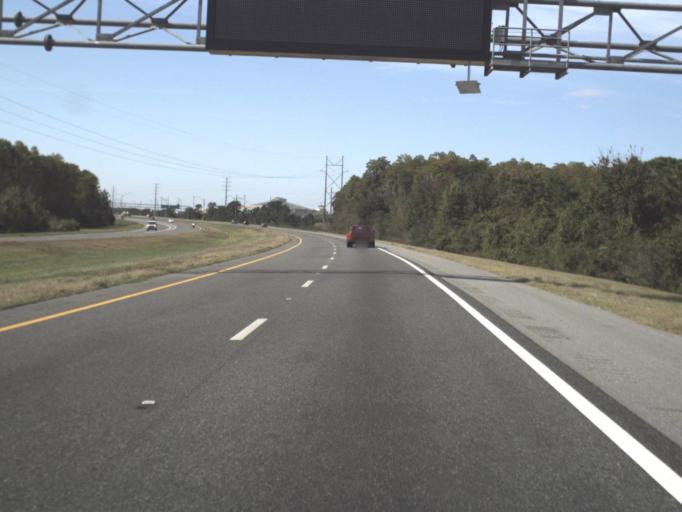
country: US
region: Florida
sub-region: Osceola County
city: Celebration
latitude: 28.3479
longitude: -81.5075
